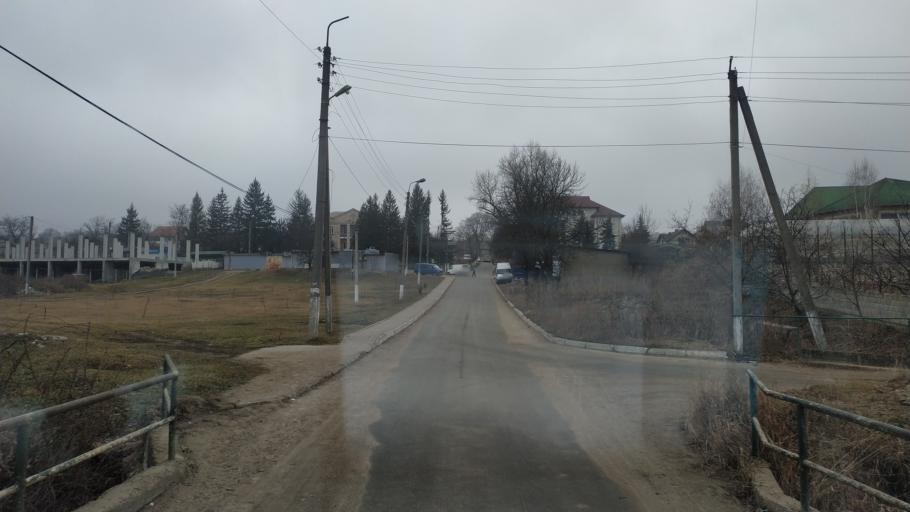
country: MD
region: Hincesti
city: Hincesti
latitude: 46.9031
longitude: 28.6742
